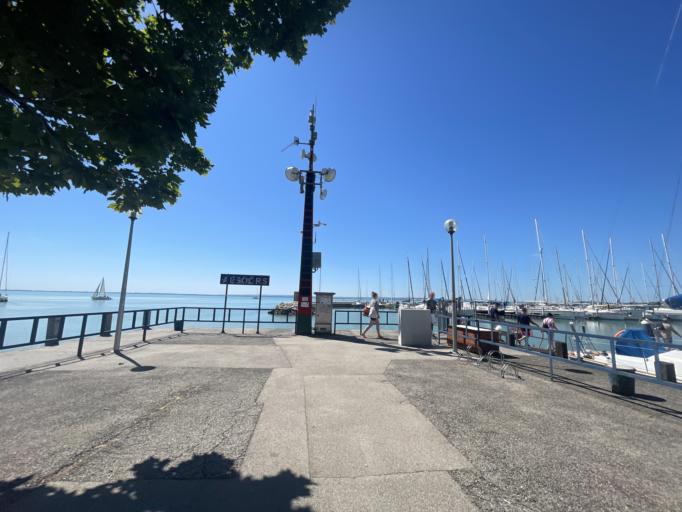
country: HU
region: Veszprem
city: Csopak
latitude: 46.9830
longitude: 17.9796
